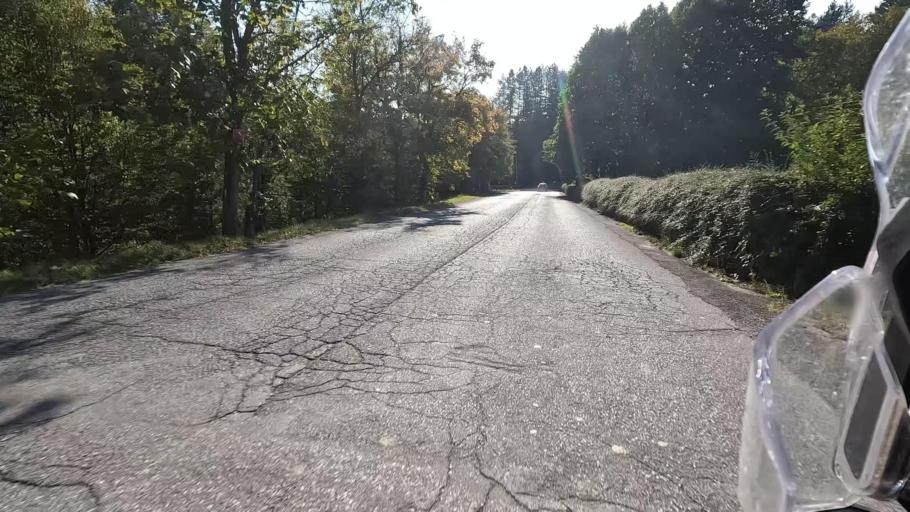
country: IT
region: Liguria
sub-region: Provincia di Savona
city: Sassello
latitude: 44.4860
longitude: 8.5045
